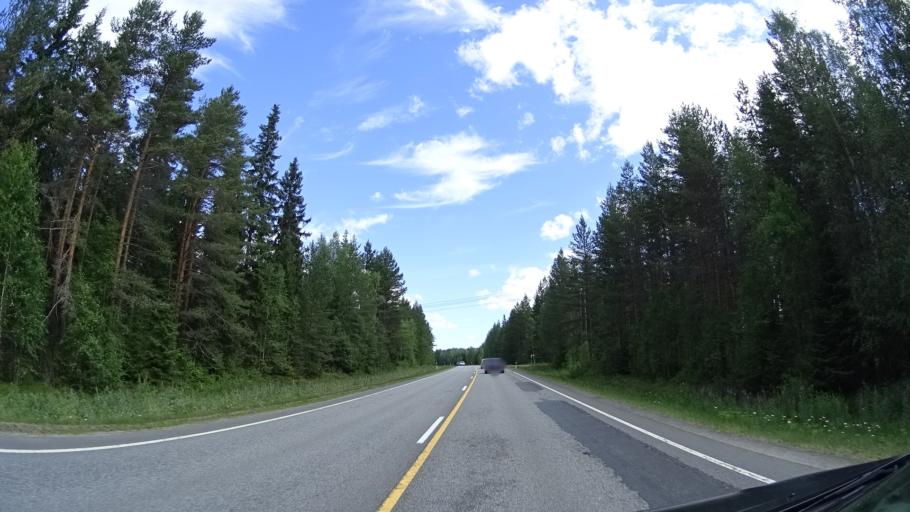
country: FI
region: Pirkanmaa
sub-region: Luoteis-Pirkanmaa
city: Kihnioe
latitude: 62.1369
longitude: 23.1428
